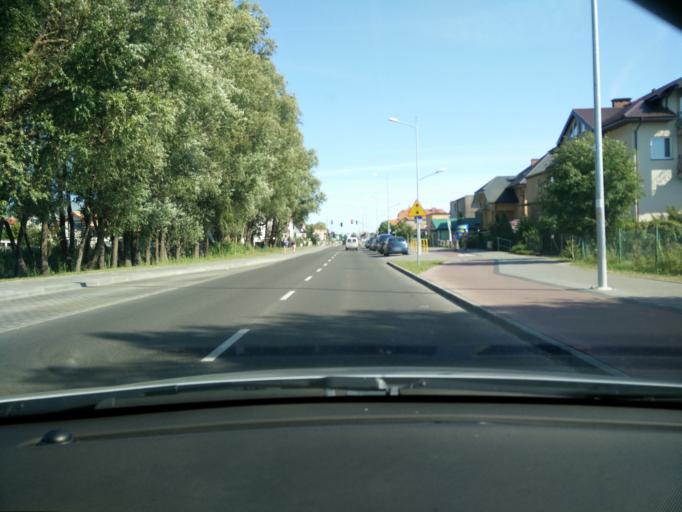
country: PL
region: Pomeranian Voivodeship
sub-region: Powiat pucki
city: Jastarnia
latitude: 54.7001
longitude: 18.6711
